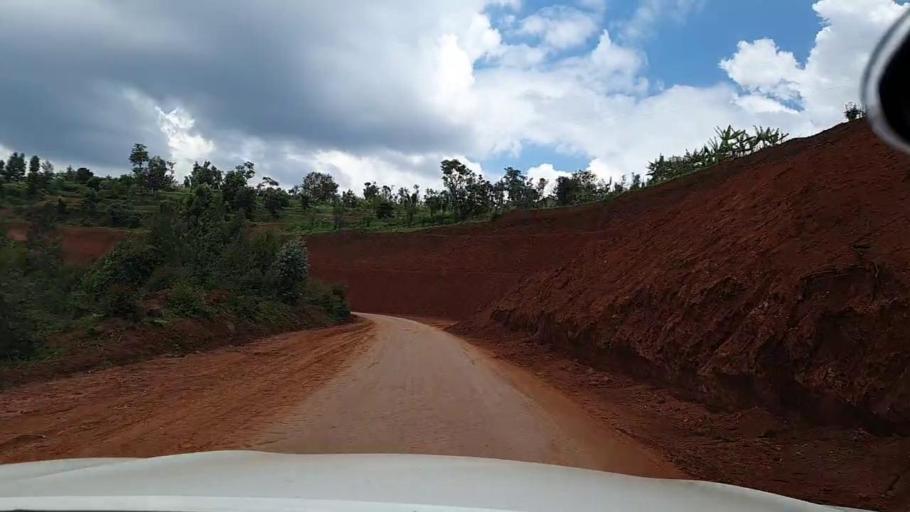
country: RW
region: Southern Province
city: Butare
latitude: -2.7071
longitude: 29.5501
